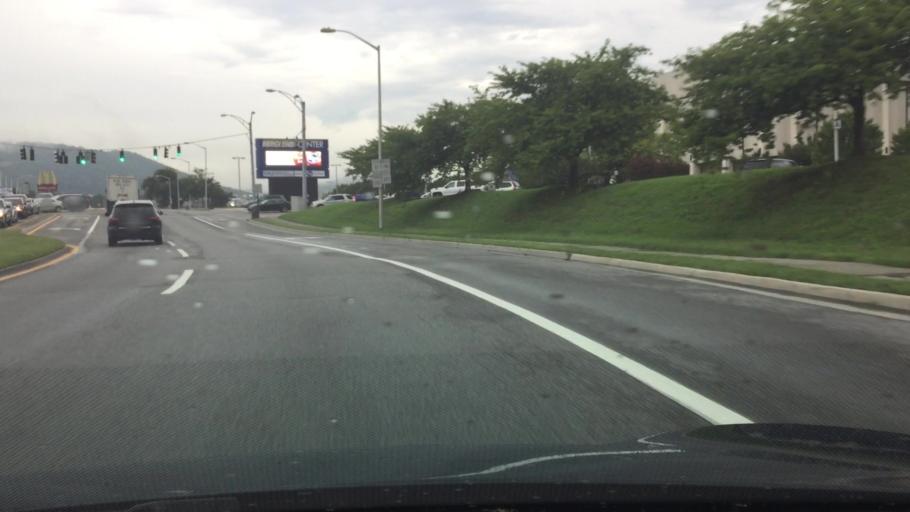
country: US
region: Virginia
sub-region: City of Roanoke
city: Roanoke
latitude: 37.2814
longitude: -79.9342
